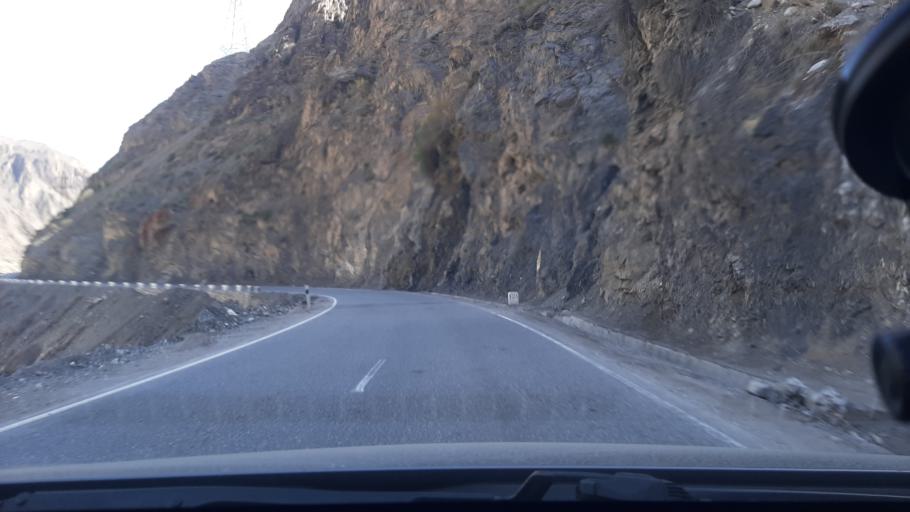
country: TJ
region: Viloyati Sughd
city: Ayni
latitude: 39.3187
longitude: 68.5461
